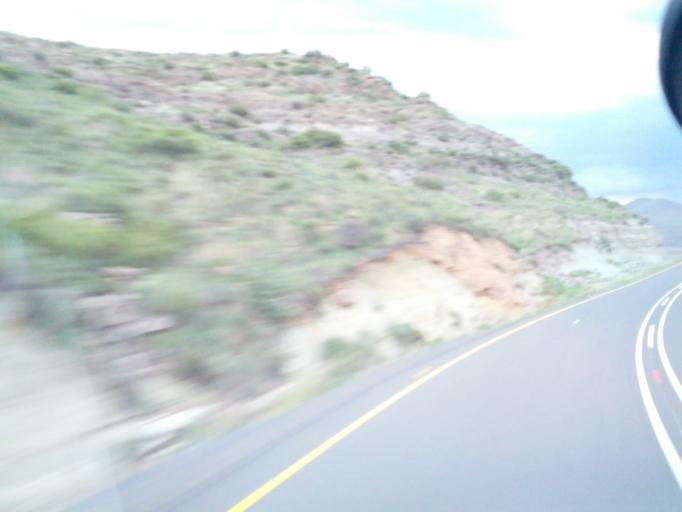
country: LS
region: Qacha's Nek
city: Qacha's Nek
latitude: -30.0363
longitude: 28.3051
